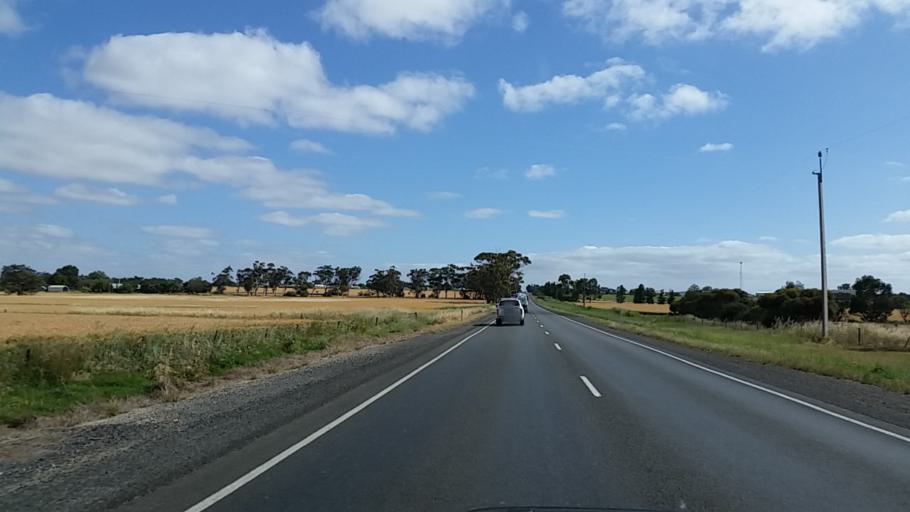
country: AU
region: South Australia
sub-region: Light
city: Roseworthy
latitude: -34.5470
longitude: 138.7489
